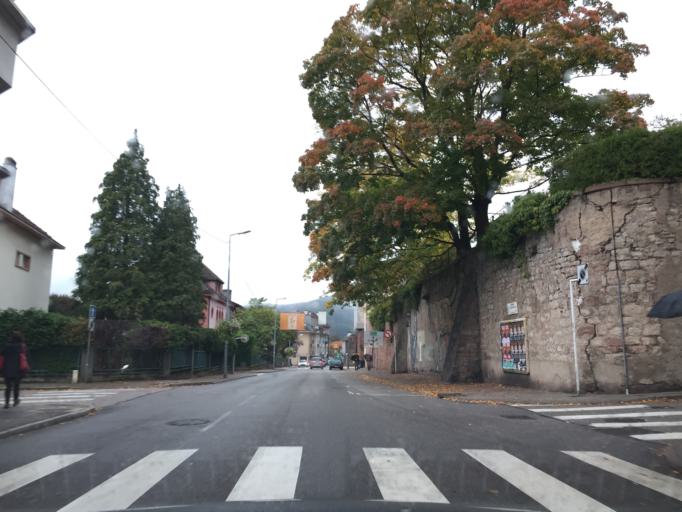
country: FR
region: Lorraine
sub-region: Departement des Vosges
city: Saint-Die-des-Vosges
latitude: 48.2881
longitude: 6.9529
